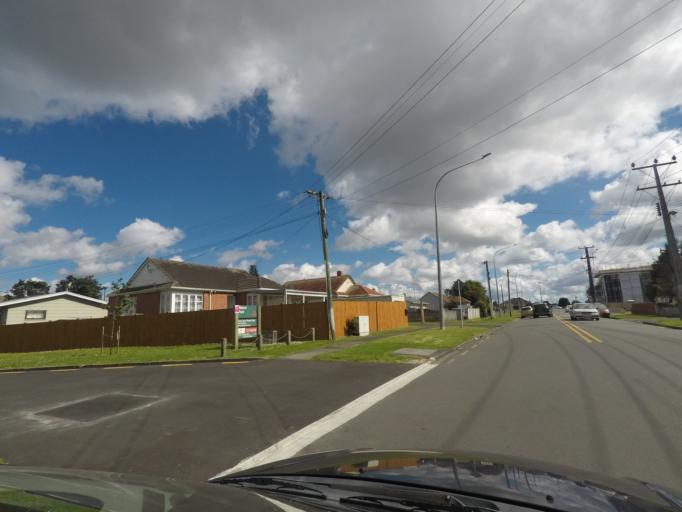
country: NZ
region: Auckland
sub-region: Auckland
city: Waitakere
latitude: -36.9107
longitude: 174.6683
